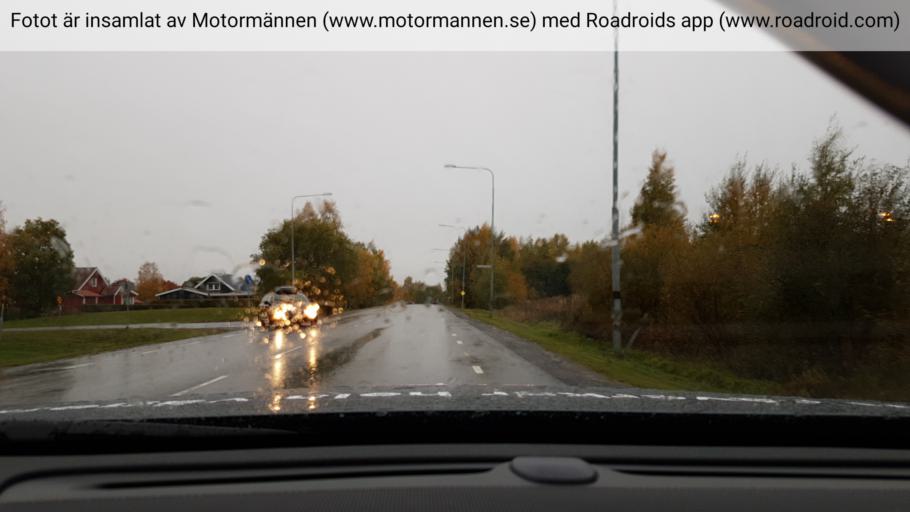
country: SE
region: Norrbotten
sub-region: Lulea Kommun
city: Sodra Sunderbyn
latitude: 65.6600
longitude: 21.9533
